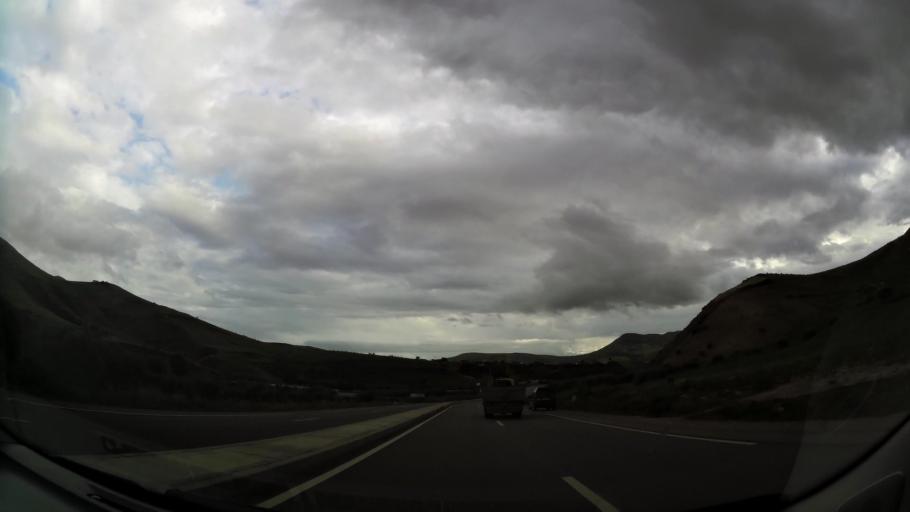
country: MA
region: Taza-Al Hoceima-Taounate
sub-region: Taza
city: Taza
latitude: 34.3159
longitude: -3.9598
